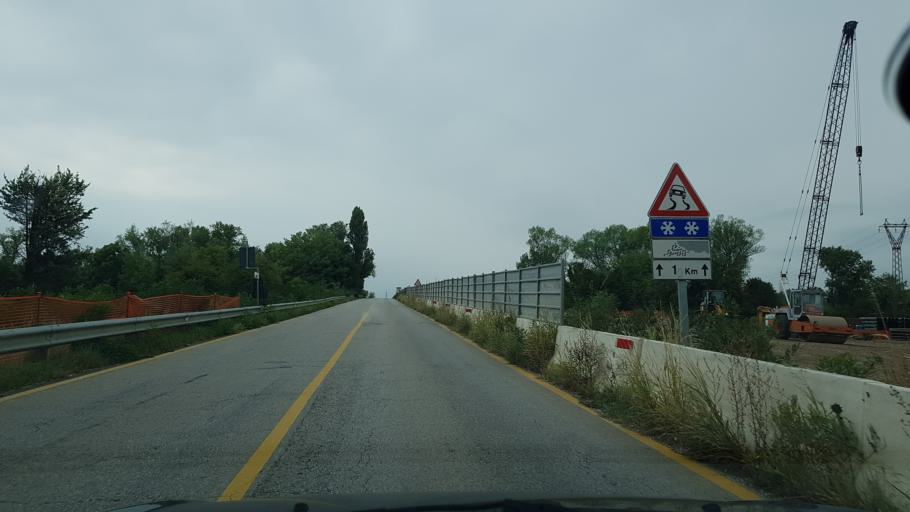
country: IT
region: Friuli Venezia Giulia
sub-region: Provincia di Udine
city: Chiopris
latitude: 45.9279
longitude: 13.3831
